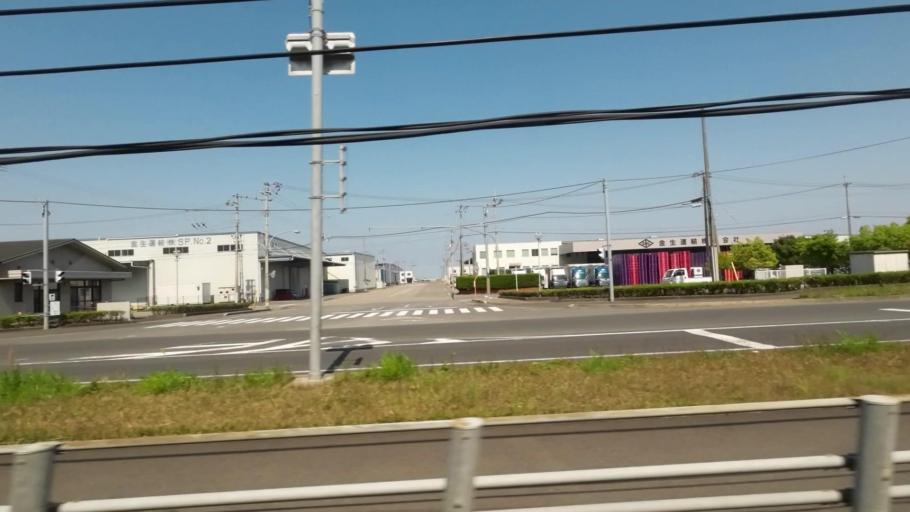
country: JP
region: Ehime
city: Kawanoecho
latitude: 34.0271
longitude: 133.5824
